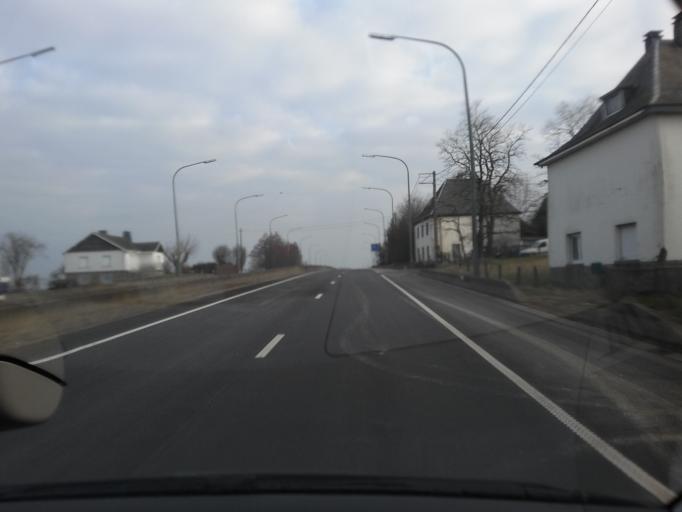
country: BE
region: Wallonia
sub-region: Province du Luxembourg
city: Fauvillers
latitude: 49.9213
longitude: 5.7039
